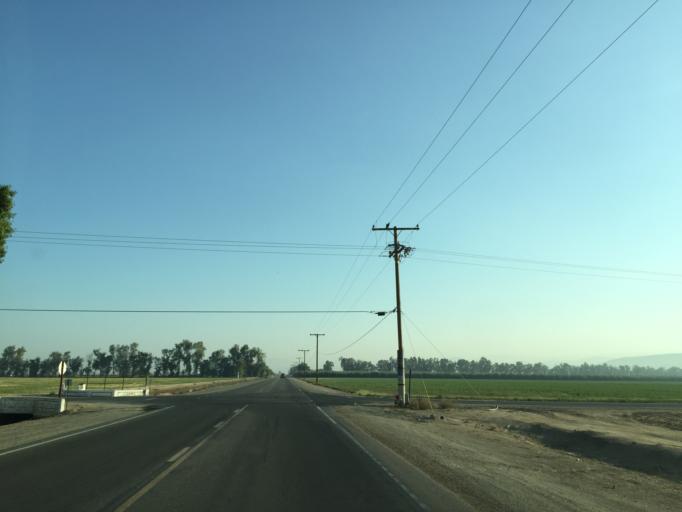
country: US
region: California
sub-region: Tulare County
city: Cutler
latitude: 36.4571
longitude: -119.2776
